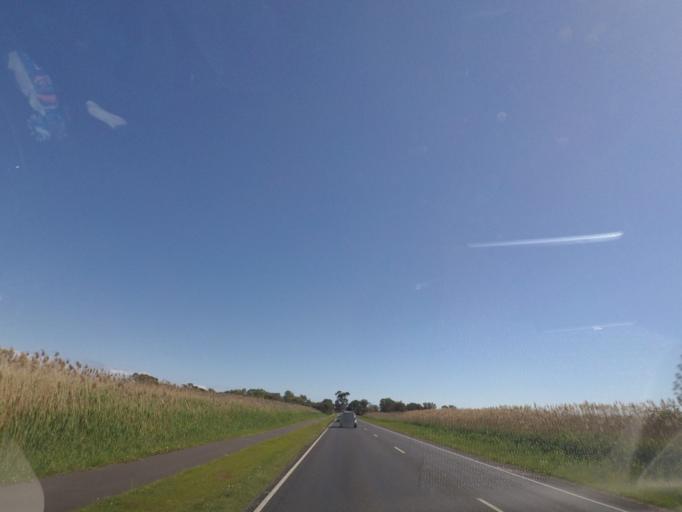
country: AU
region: Victoria
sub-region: Kingston
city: Chelsea Heights
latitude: -38.0321
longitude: 145.1255
